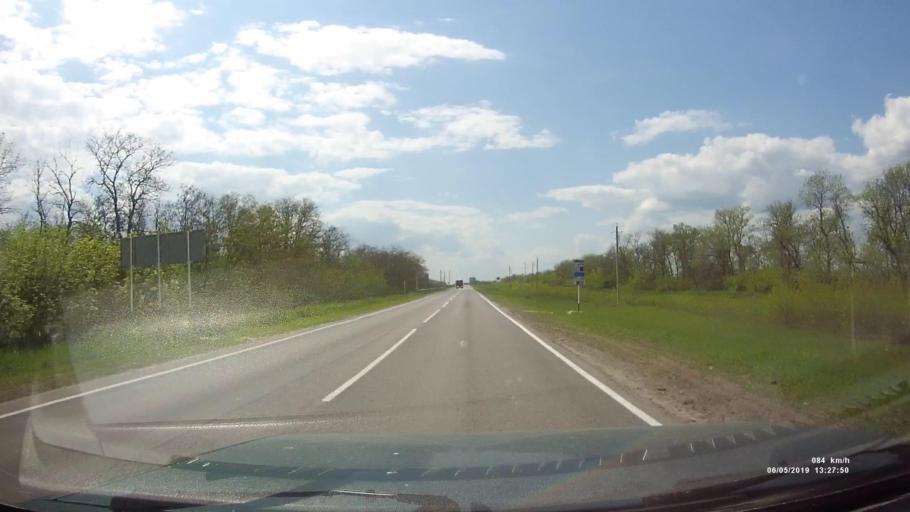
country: RU
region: Rostov
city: Ust'-Donetskiy
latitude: 47.6714
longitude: 40.8731
